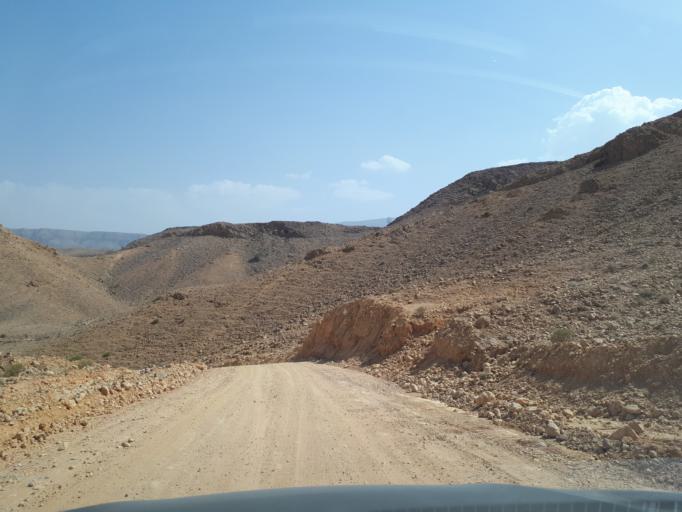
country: OM
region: Ash Sharqiyah
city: Ibra'
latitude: 23.0875
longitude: 58.9488
